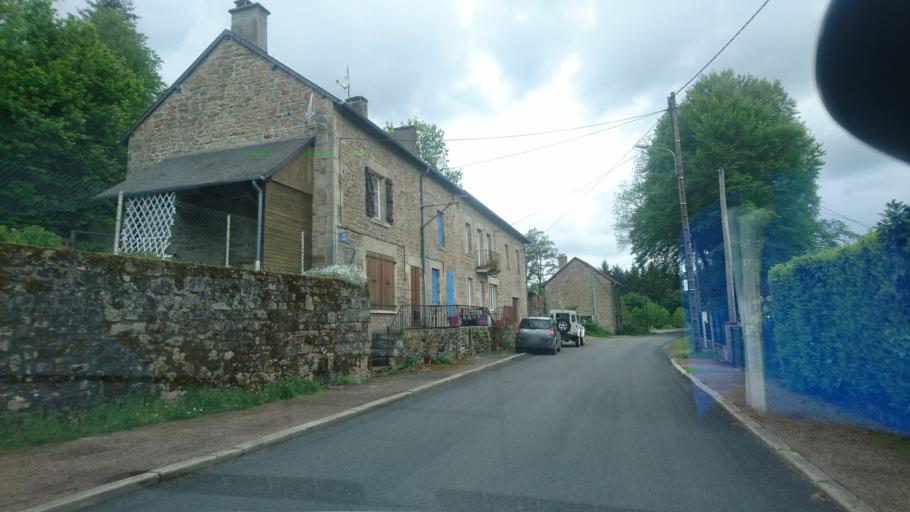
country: FR
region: Limousin
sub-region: Departement de la Haute-Vienne
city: Peyrat-le-Chateau
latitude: 45.8421
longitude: 1.9080
